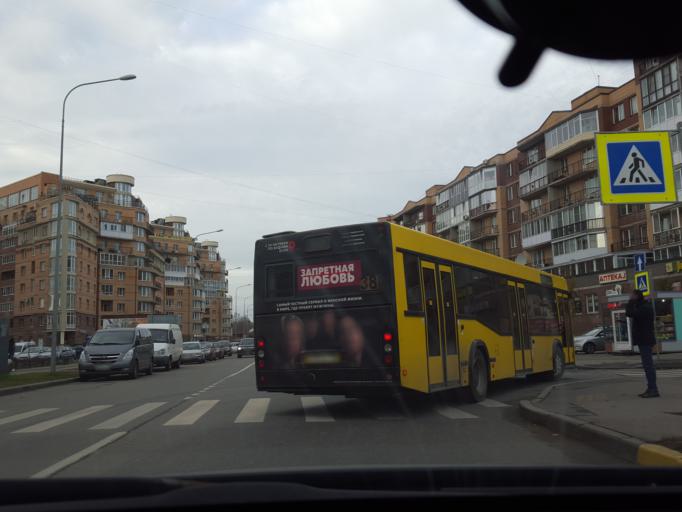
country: RU
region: St.-Petersburg
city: Ozerki
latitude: 60.0328
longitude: 30.2994
